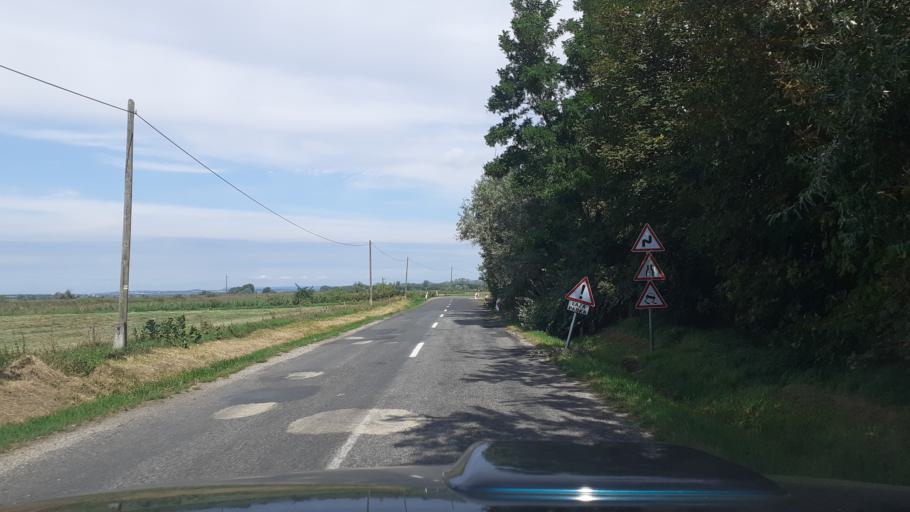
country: HU
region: Fejer
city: Seregelyes
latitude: 47.1394
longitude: 18.5759
